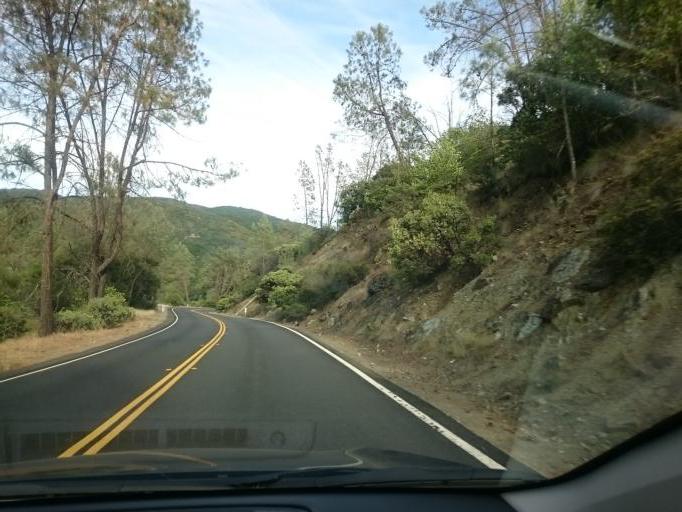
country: US
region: California
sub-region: Napa County
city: Yountville
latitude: 38.4953
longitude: -122.2491
